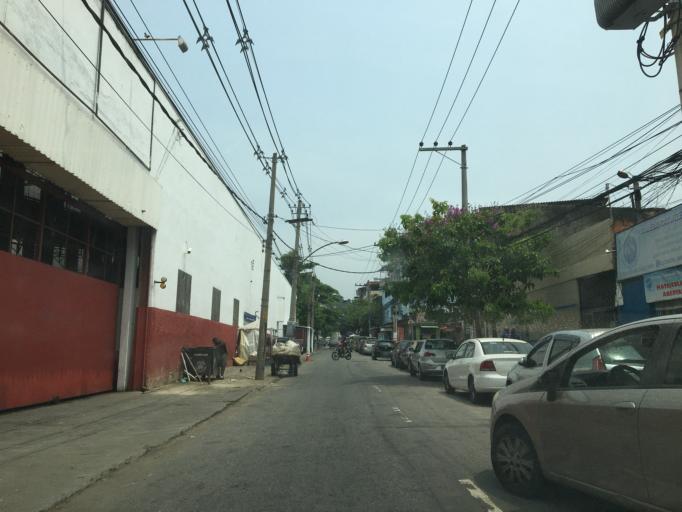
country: BR
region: Rio de Janeiro
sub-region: Rio De Janeiro
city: Rio de Janeiro
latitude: -22.8887
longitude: -43.2270
